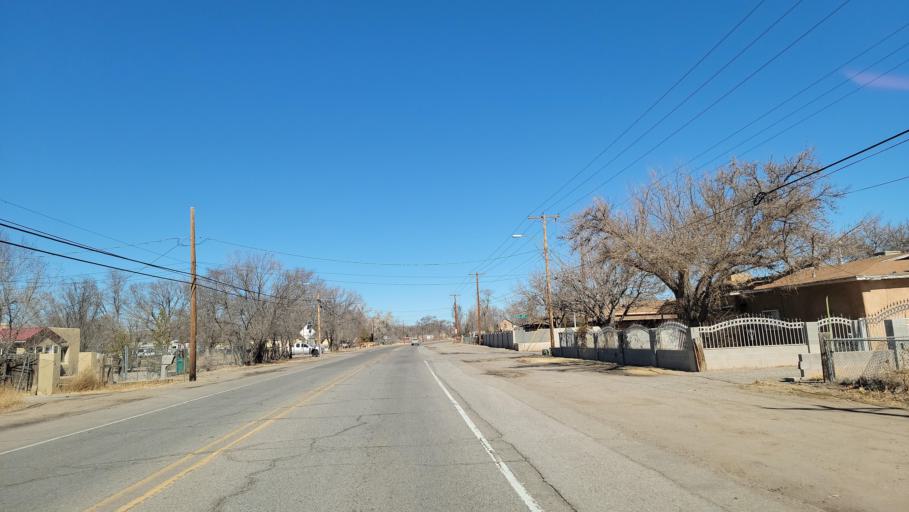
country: US
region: New Mexico
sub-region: Bernalillo County
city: South Valley
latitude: 34.9814
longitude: -106.6971
